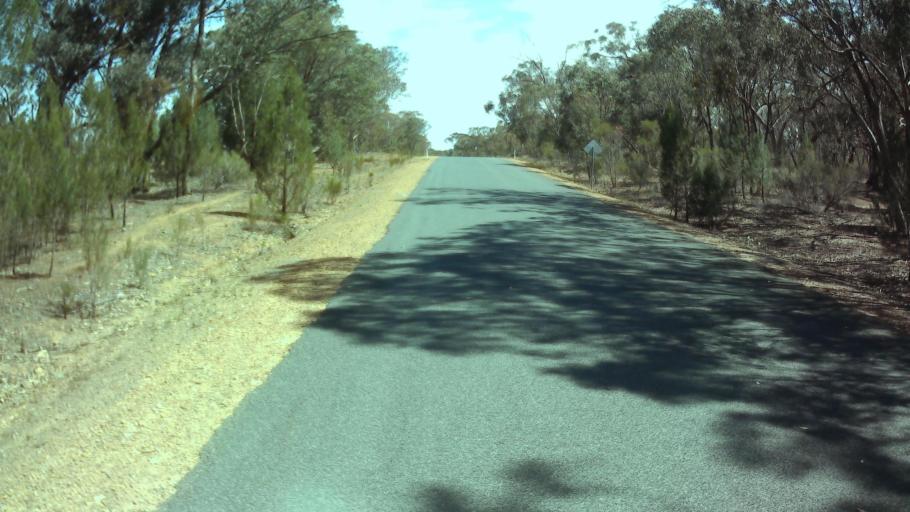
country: AU
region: New South Wales
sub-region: Weddin
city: Grenfell
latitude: -34.0035
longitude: 148.1305
